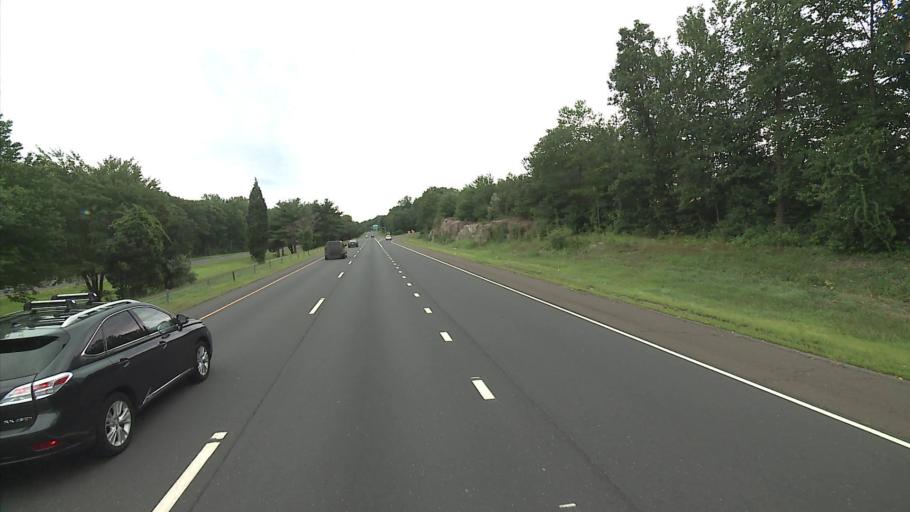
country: US
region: Connecticut
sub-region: Fairfield County
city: Shelton
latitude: 41.2623
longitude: -73.1332
